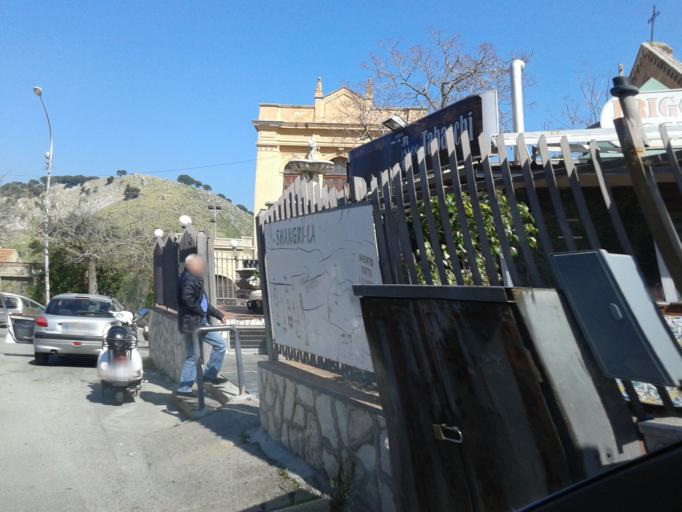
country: IT
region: Sicily
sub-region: Palermo
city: Piano dei Geli
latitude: 38.1141
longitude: 13.2964
